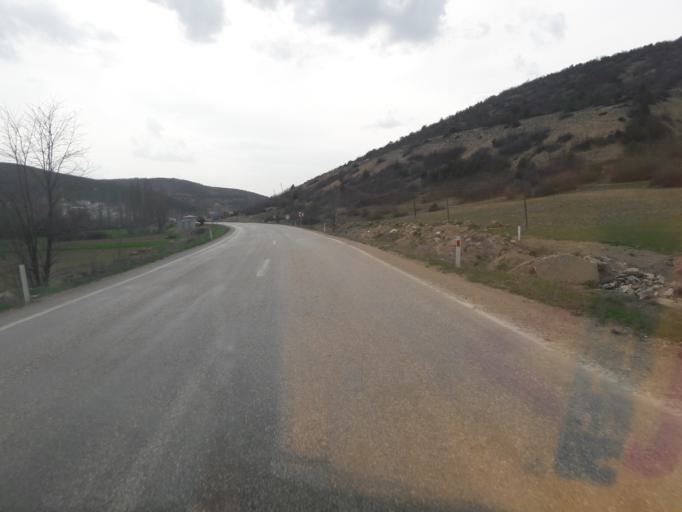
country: TR
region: Gumushane
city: Siran
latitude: 40.1771
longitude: 39.1416
